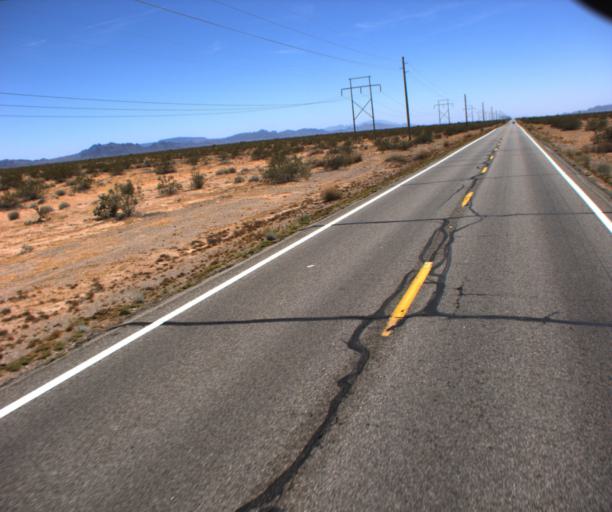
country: US
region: Arizona
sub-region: La Paz County
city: Quartzsite
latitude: 33.8769
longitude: -114.2170
